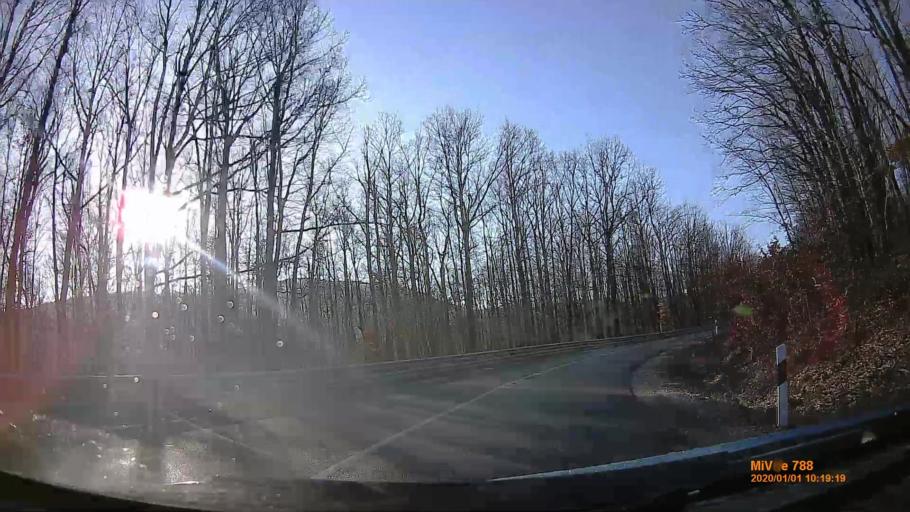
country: HU
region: Heves
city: Paradsasvar
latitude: 47.9045
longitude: 19.9963
